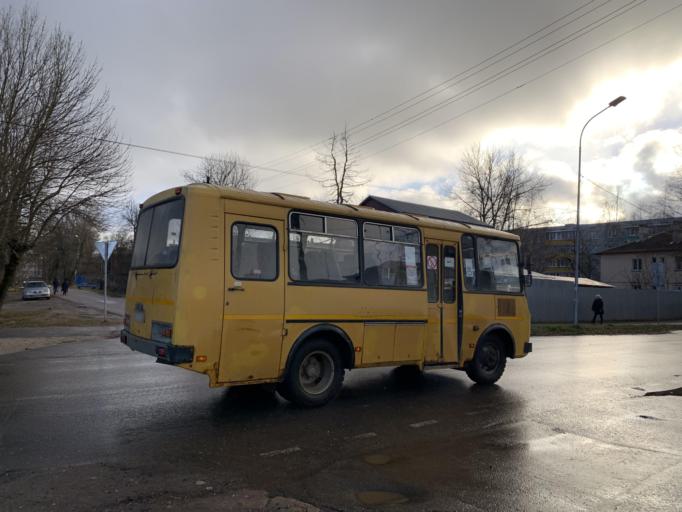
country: RU
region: Tverskaya
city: Likhoslavl'
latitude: 57.1259
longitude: 35.4626
